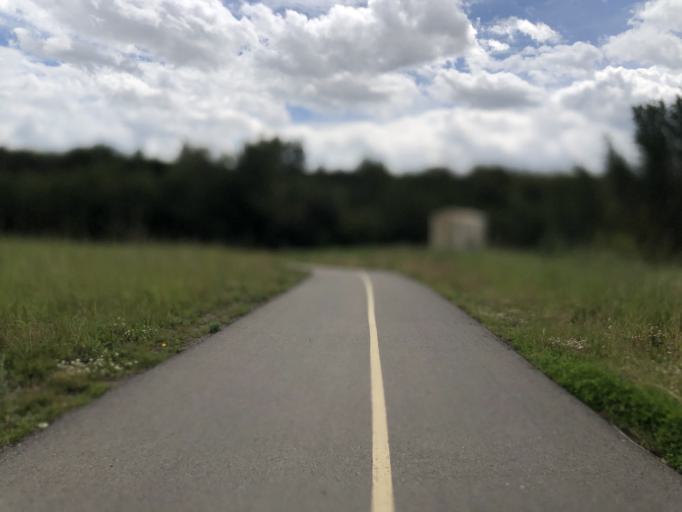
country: CA
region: Alberta
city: Calgary
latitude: 51.0036
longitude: -114.0209
